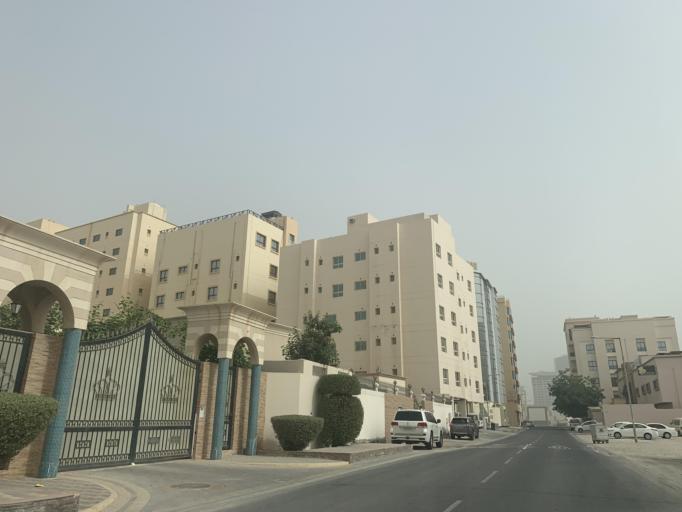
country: BH
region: Manama
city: Jidd Hafs
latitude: 26.2251
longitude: 50.5540
